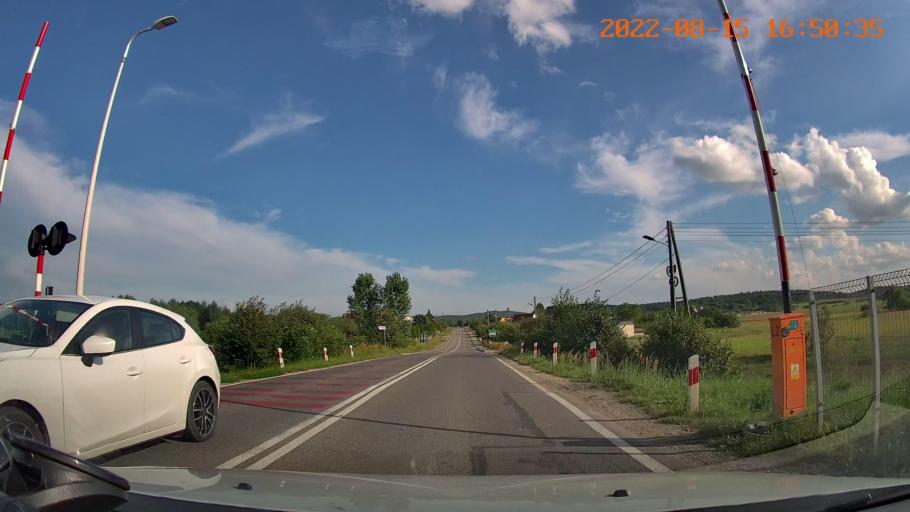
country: PL
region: Swietokrzyskie
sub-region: Powiat kielecki
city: Piekoszow
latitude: 50.8723
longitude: 20.4721
